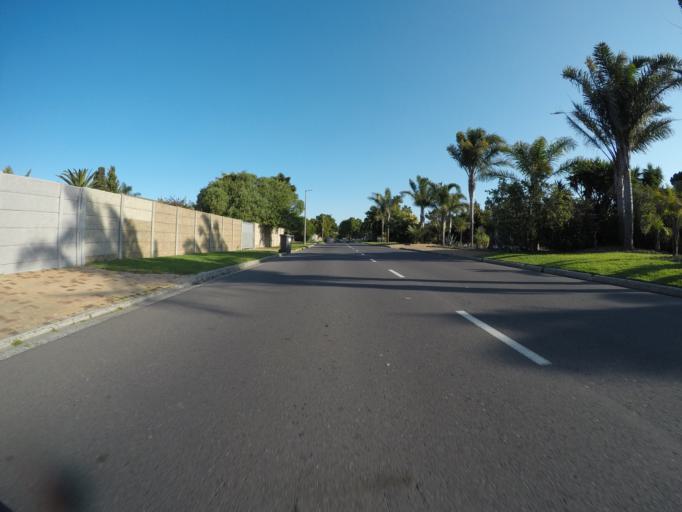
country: ZA
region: Western Cape
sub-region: City of Cape Town
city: Kraaifontein
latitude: -33.8512
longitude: 18.6577
